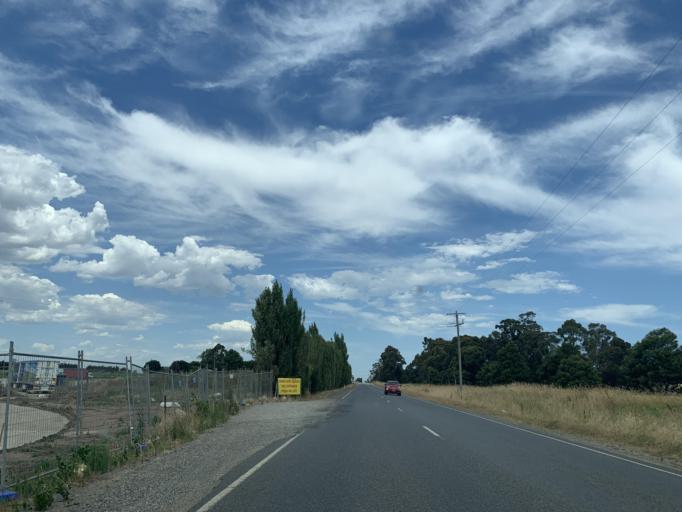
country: AU
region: Victoria
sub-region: Casey
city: Junction Village
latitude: -38.1305
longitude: 145.3295
